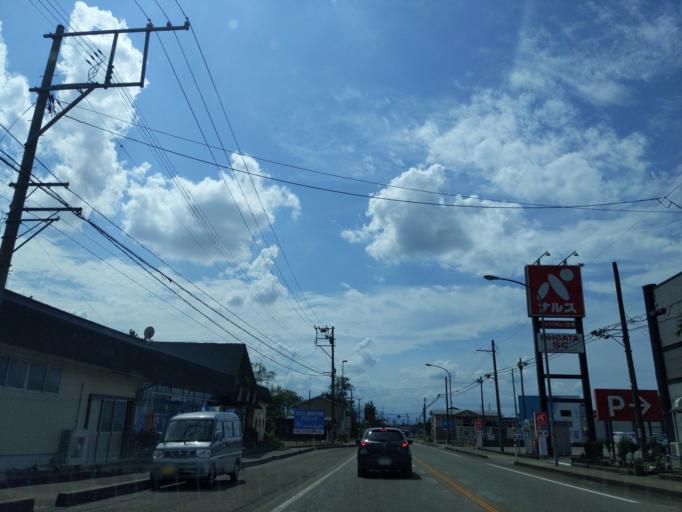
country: JP
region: Niigata
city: Joetsu
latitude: 37.2286
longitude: 138.3322
